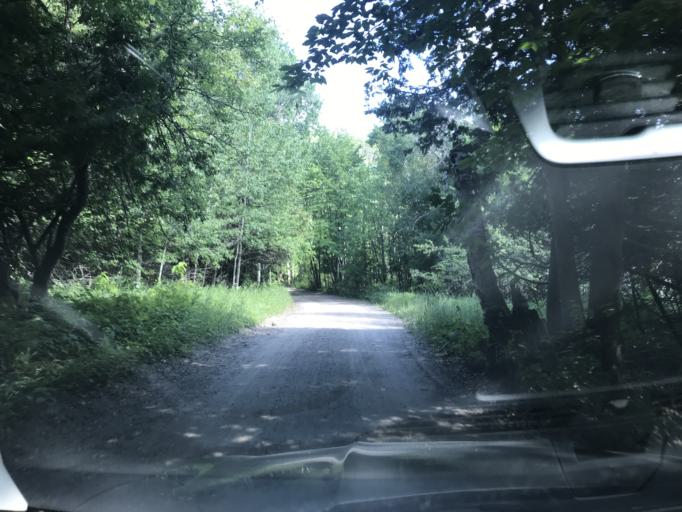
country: US
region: Michigan
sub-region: Cheboygan County
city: Cheboygan
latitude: 45.6222
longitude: -84.6769
